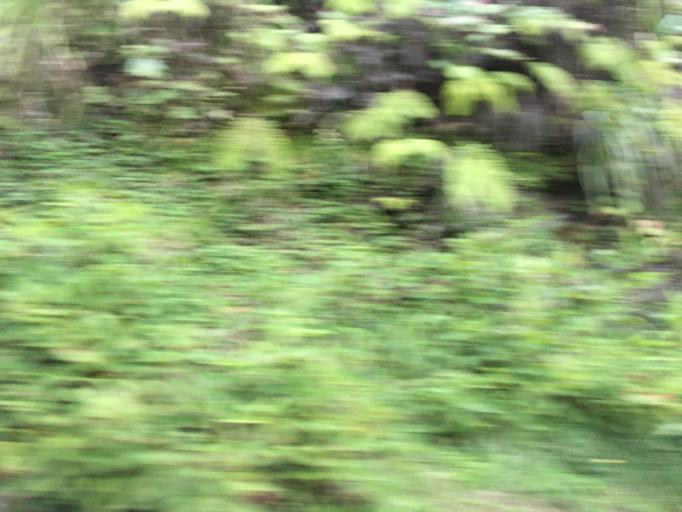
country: TW
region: Taiwan
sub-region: Yilan
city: Yilan
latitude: 24.5124
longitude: 121.5938
